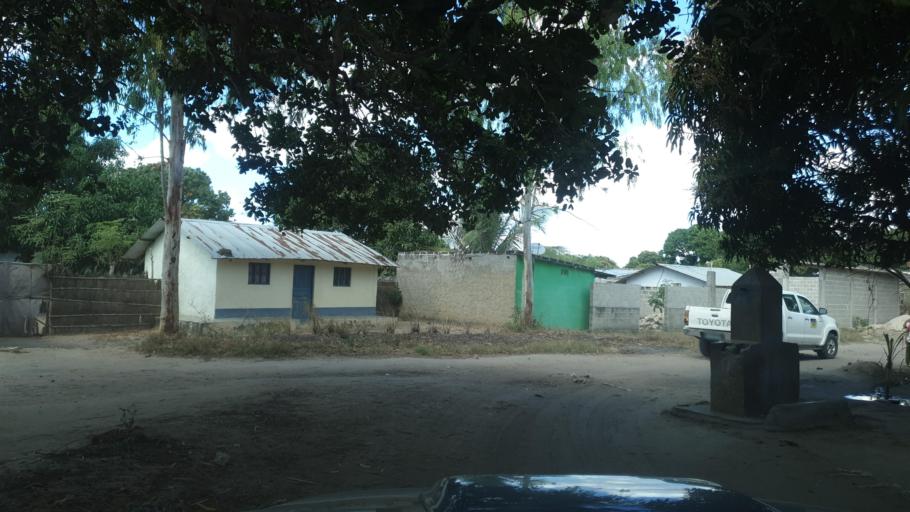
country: MZ
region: Nampula
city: Nacala
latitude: -14.5682
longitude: 40.7005
